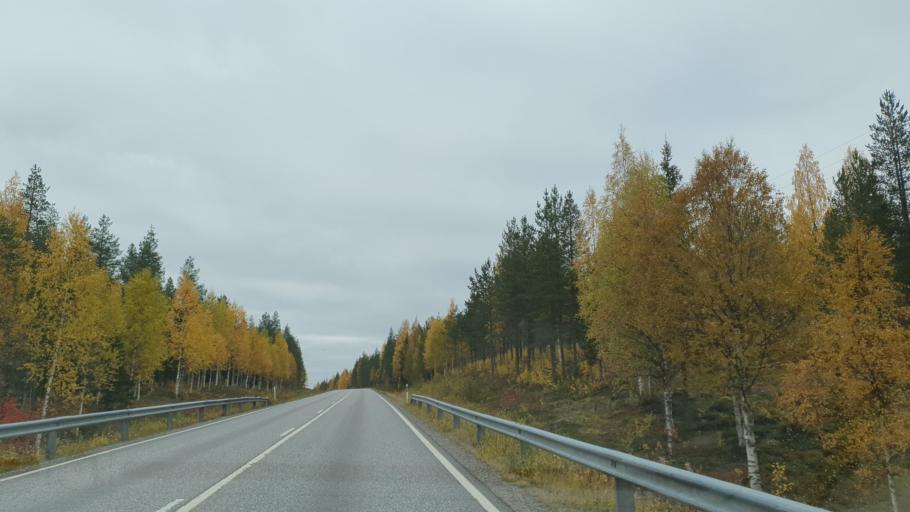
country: FI
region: Lapland
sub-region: Rovaniemi
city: Rovaniemi
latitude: 66.2557
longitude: 26.1549
